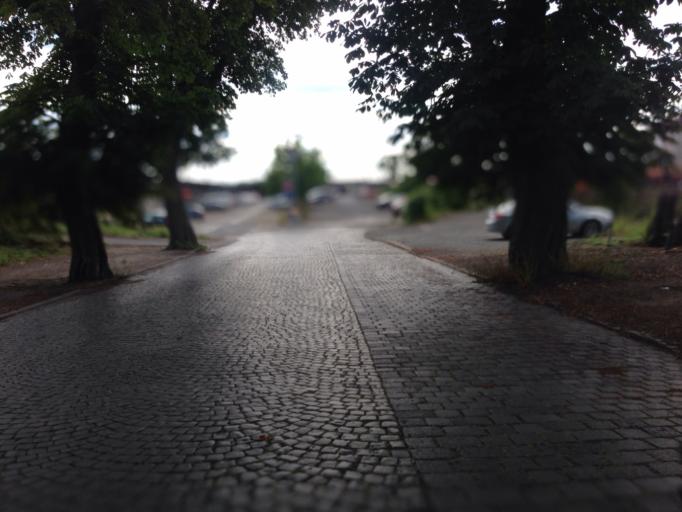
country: DE
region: Hesse
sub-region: Regierungsbezirk Darmstadt
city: Hanau am Main
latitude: 50.1222
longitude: 8.9268
